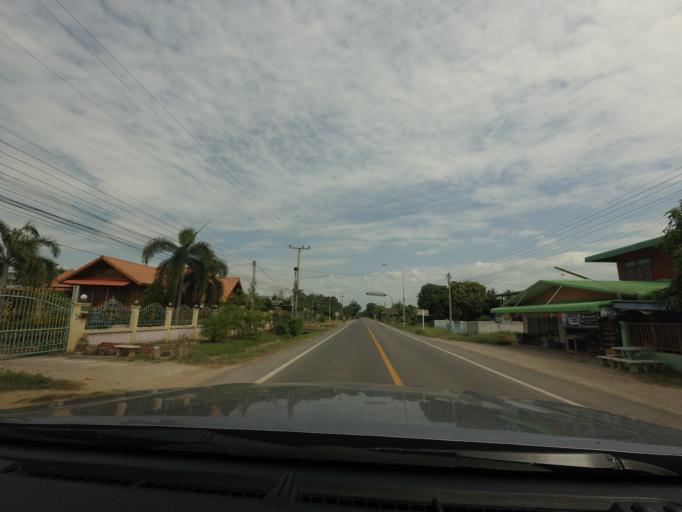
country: TH
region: Phitsanulok
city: Wang Thong
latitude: 16.7208
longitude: 100.3691
